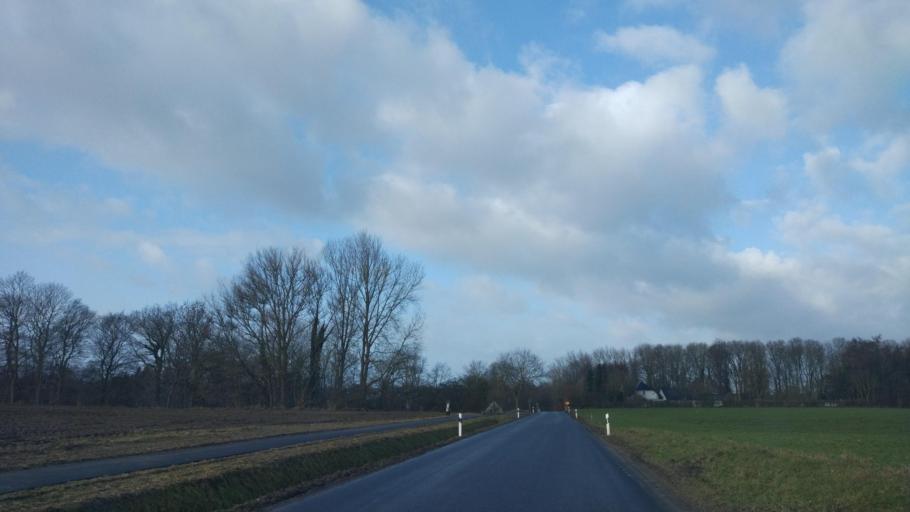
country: DE
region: Schleswig-Holstein
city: Taarstedt
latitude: 54.5616
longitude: 9.6855
